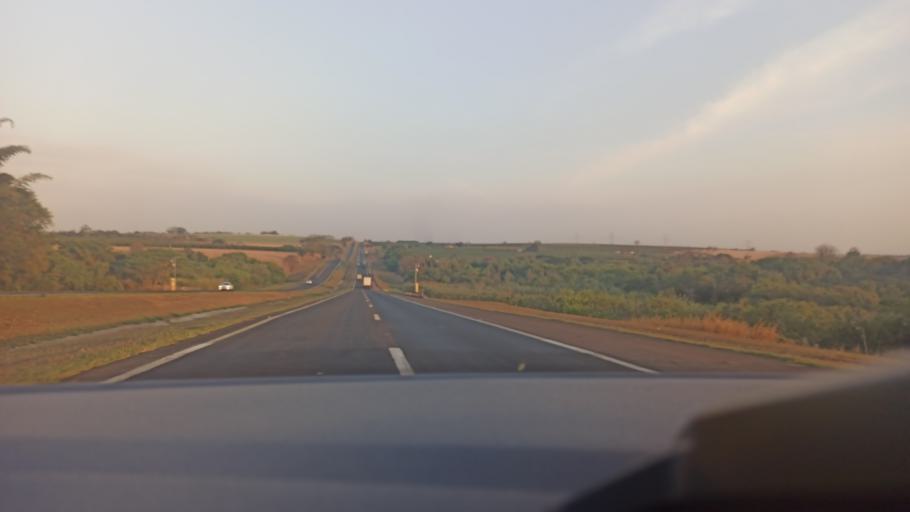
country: BR
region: Sao Paulo
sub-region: Santa Adelia
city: Santa Adelia
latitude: -21.3919
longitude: -48.7195
